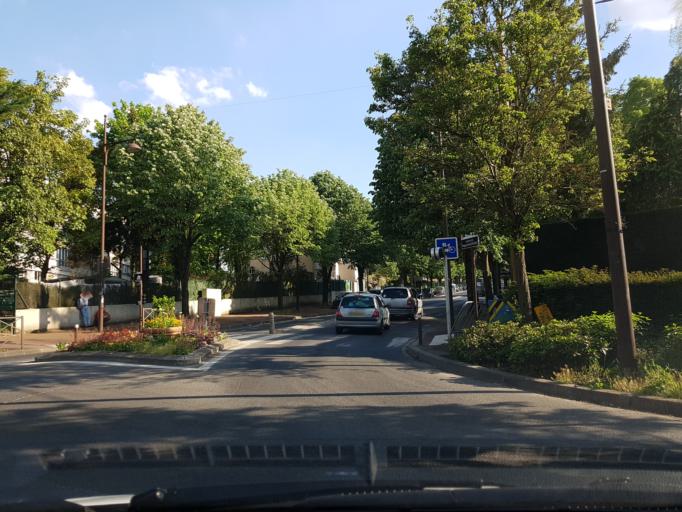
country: FR
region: Ile-de-France
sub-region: Departement des Hauts-de-Seine
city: Chatenay-Malabry
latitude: 48.7701
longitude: 2.2740
